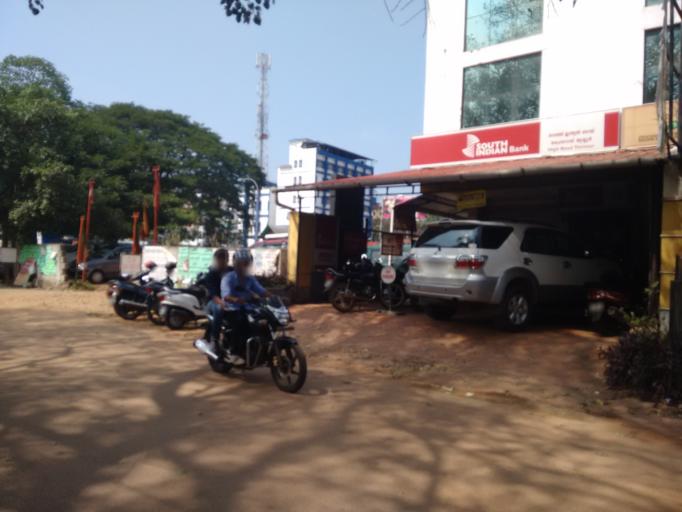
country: IN
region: Kerala
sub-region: Thrissur District
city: Trichur
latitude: 10.5191
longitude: 76.2164
